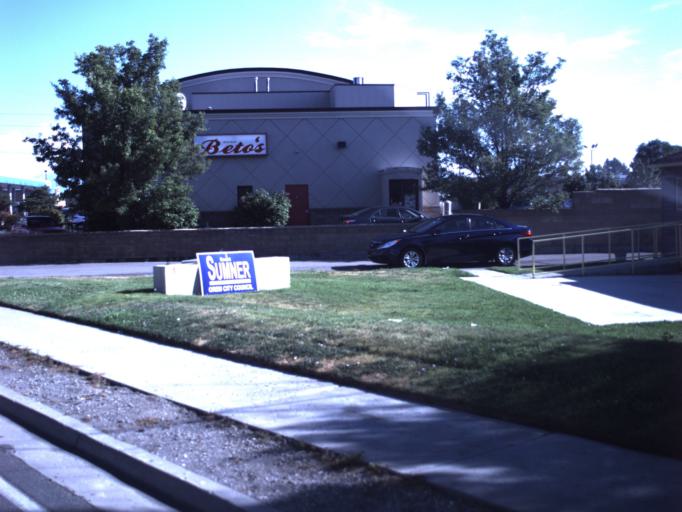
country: US
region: Utah
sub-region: Utah County
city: Lindon
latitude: 40.3281
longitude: -111.7090
